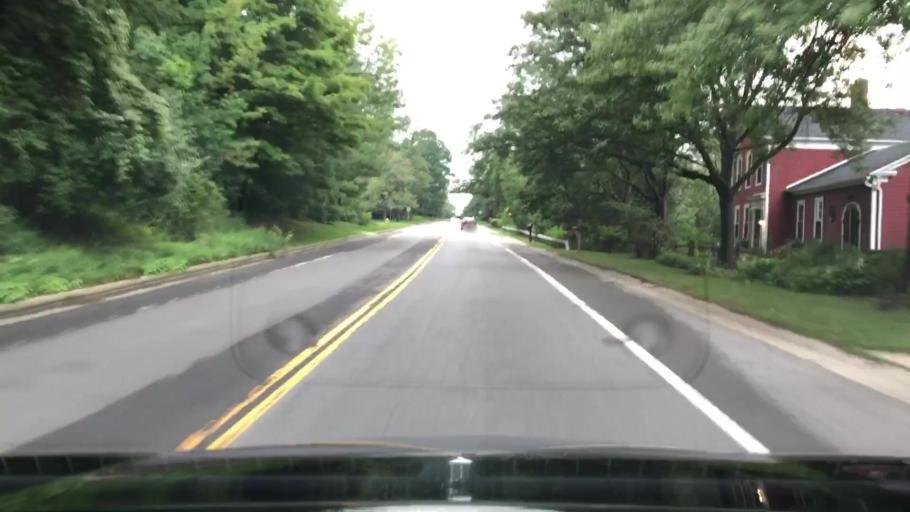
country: US
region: New York
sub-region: Erie County
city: Orchard Park
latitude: 42.7530
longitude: -78.6975
